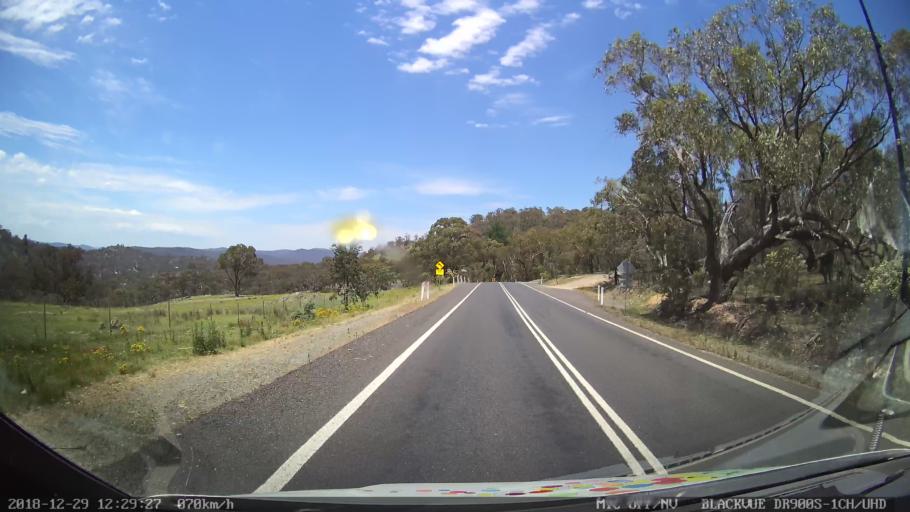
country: AU
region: Australian Capital Territory
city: Macarthur
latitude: -35.4980
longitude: 149.2308
